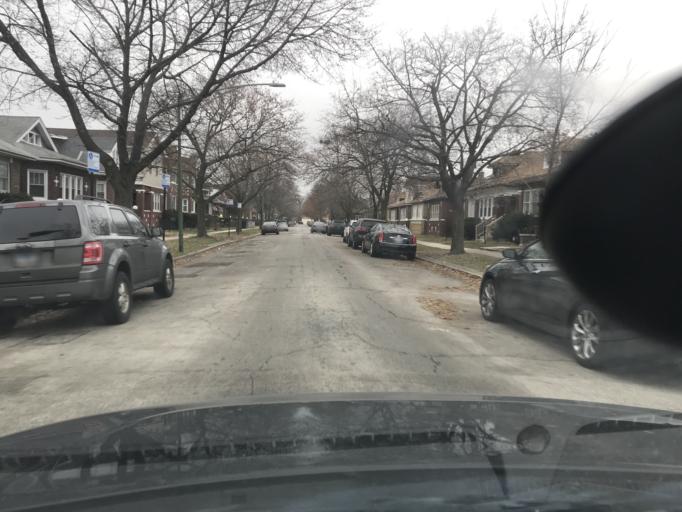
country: US
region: Indiana
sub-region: Lake County
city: Whiting
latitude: 41.7439
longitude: -87.5710
